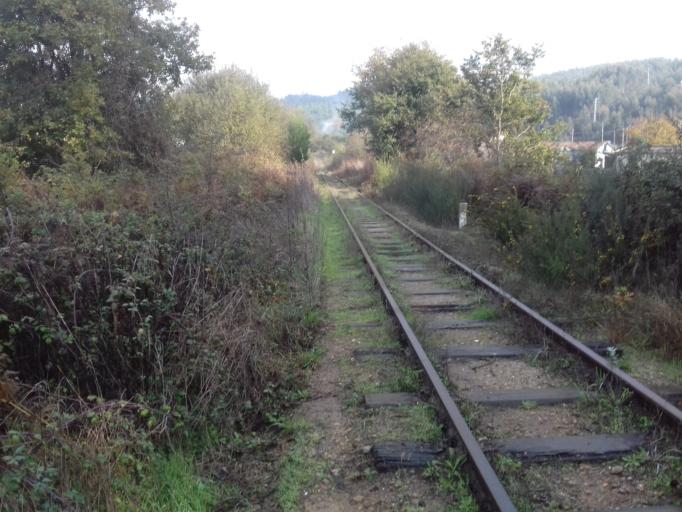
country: PT
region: Aveiro
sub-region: Albergaria-A-Velha
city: Branca
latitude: 40.7779
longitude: -8.4861
